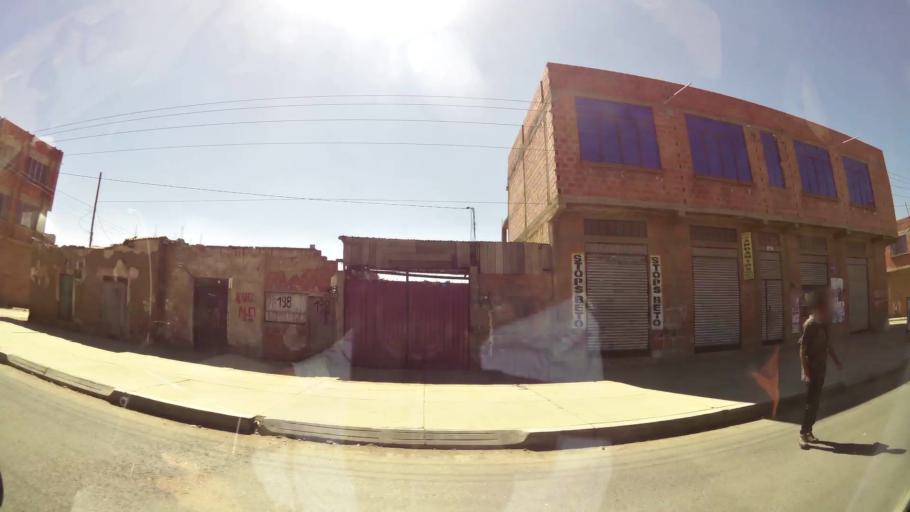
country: BO
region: La Paz
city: La Paz
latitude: -16.5364
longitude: -68.2049
